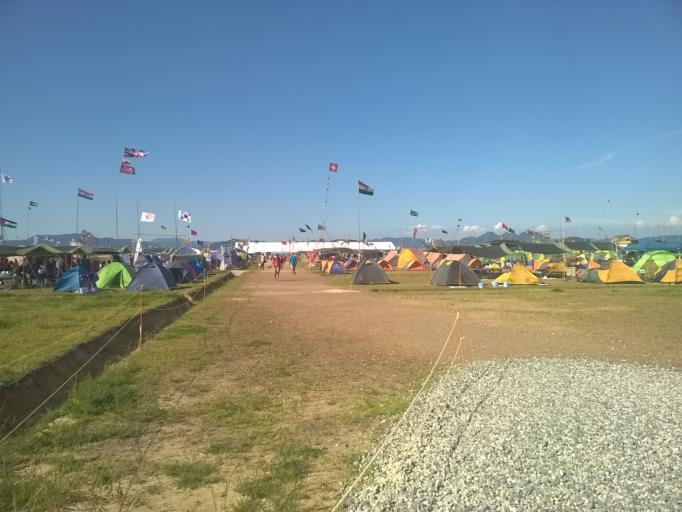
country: JP
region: Yamaguchi
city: Ogori-shimogo
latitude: 34.0122
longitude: 131.3719
